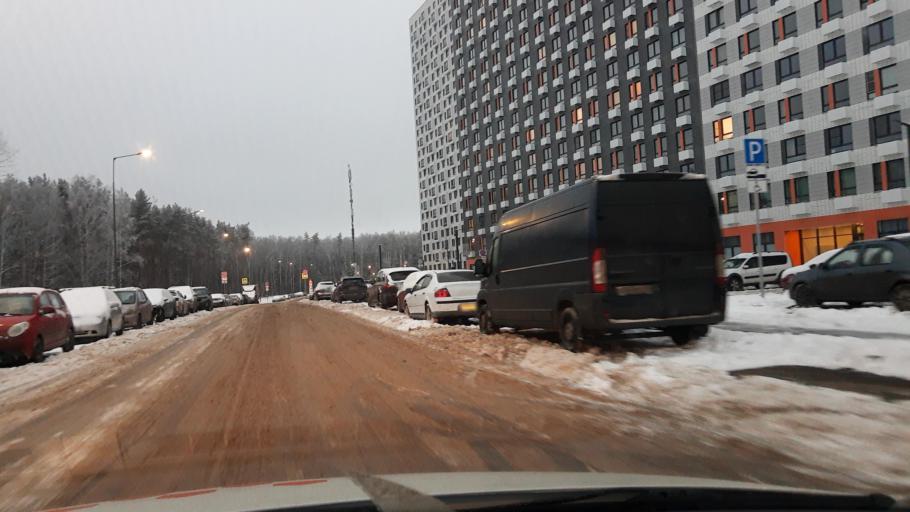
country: RU
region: Moscow
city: Solntsevo
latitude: 55.6166
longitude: 37.4067
